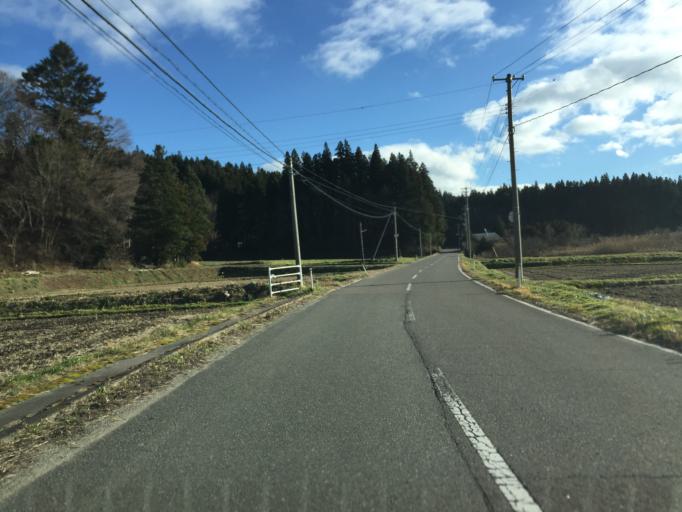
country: JP
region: Fukushima
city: Funehikimachi-funehiki
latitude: 37.2490
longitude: 140.6701
